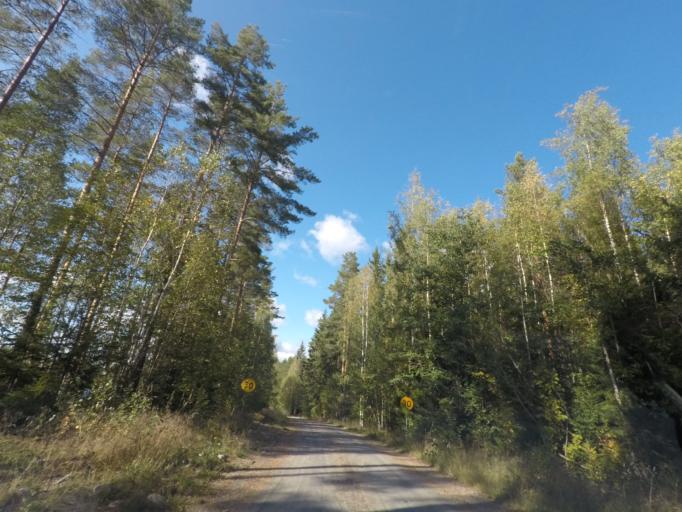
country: SE
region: Vaestmanland
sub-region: Skinnskattebergs Kommun
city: Skinnskatteberg
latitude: 59.8292
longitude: 15.5120
